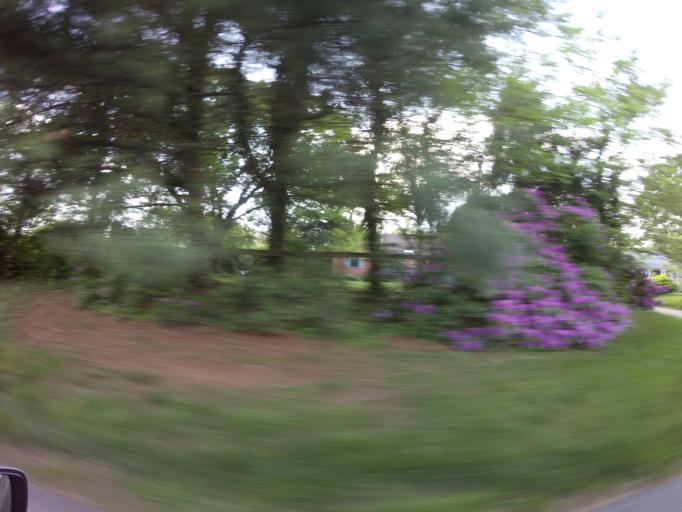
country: US
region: Maryland
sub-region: Baltimore County
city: Cockeysville
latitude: 39.4867
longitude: -76.7078
